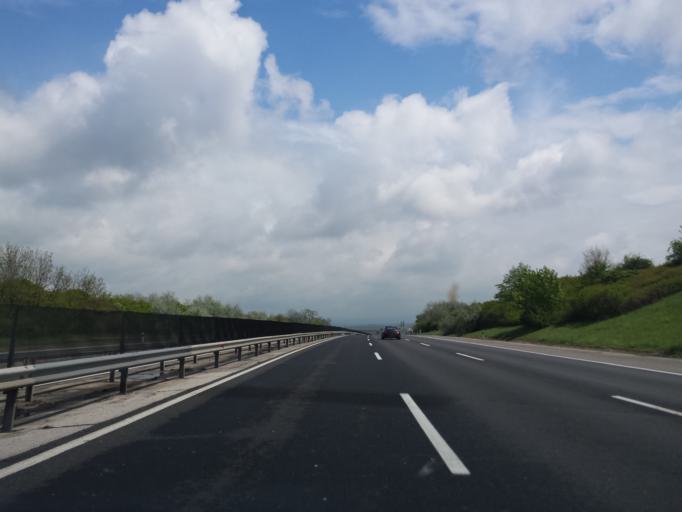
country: HU
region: Fejer
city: Many
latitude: 47.5110
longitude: 18.6503
